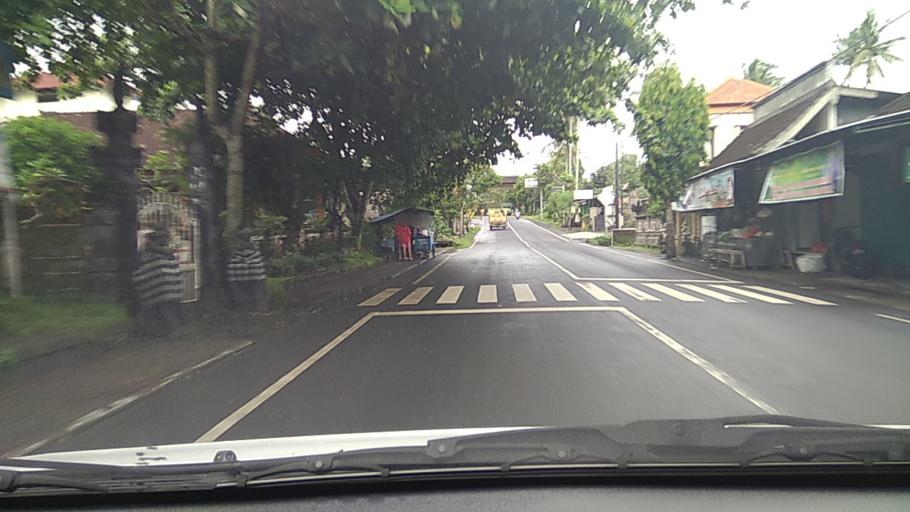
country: ID
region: Bali
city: Banjar Budakeling
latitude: -8.4347
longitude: 115.5898
